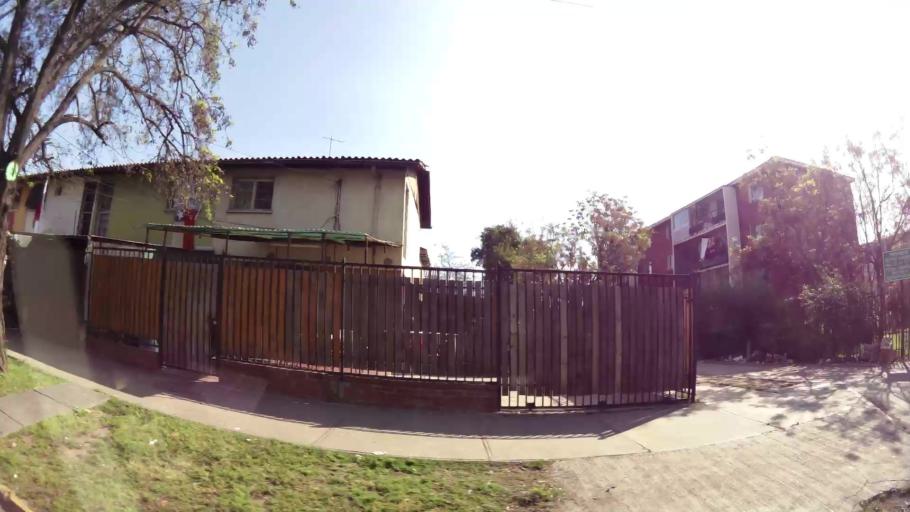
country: CL
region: Santiago Metropolitan
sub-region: Provincia de Santiago
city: Villa Presidente Frei, Nunoa, Santiago, Chile
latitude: -33.4666
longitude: -70.6146
